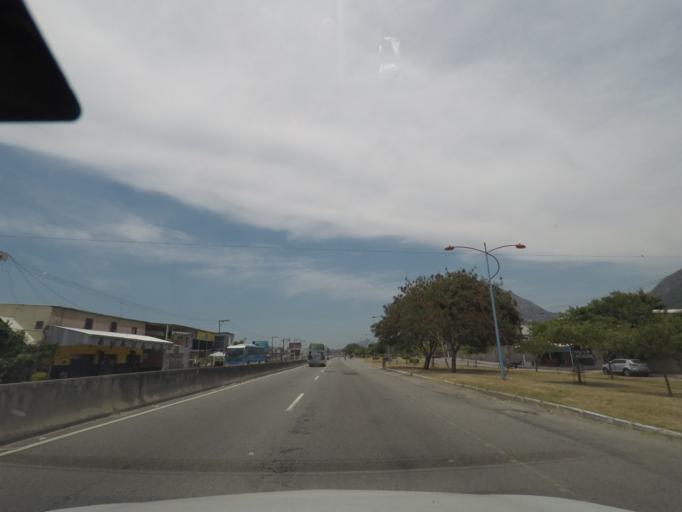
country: BR
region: Rio de Janeiro
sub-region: Marica
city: Marica
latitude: -22.9321
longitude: -42.8858
